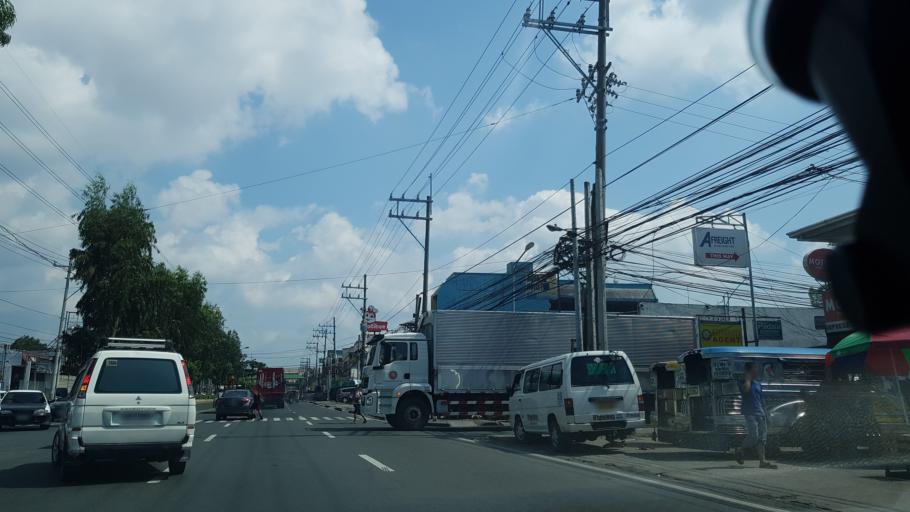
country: PH
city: Sambayanihan People's Village
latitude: 14.4810
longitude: 120.9967
